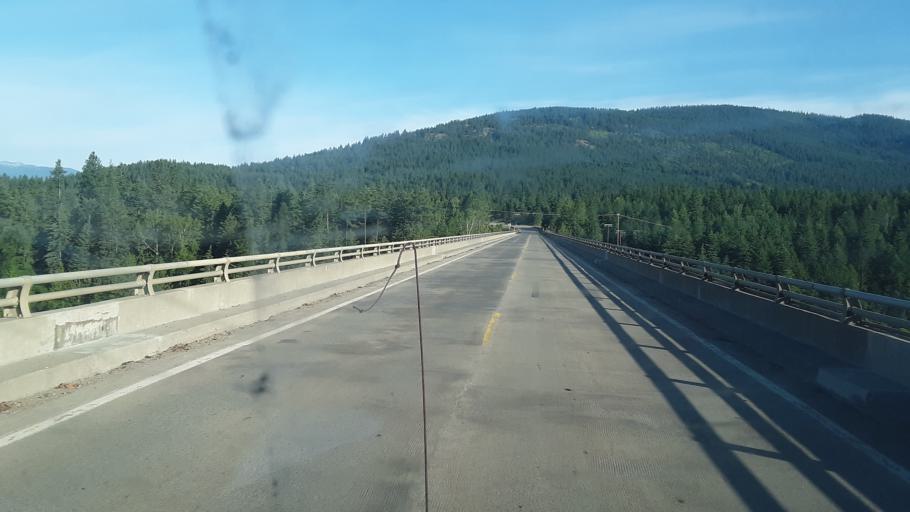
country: US
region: Idaho
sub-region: Boundary County
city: Bonners Ferry
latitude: 48.7284
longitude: -116.1777
